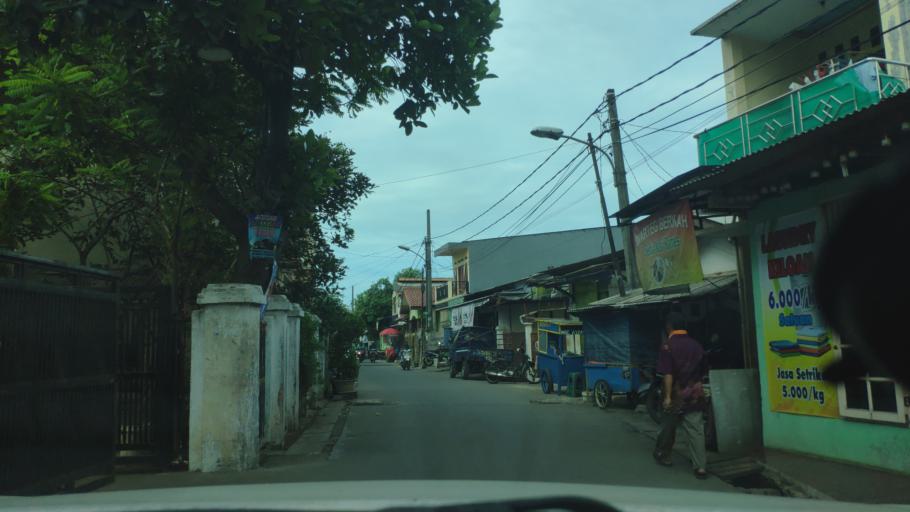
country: ID
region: West Java
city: Ciputat
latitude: -6.2216
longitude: 106.7132
